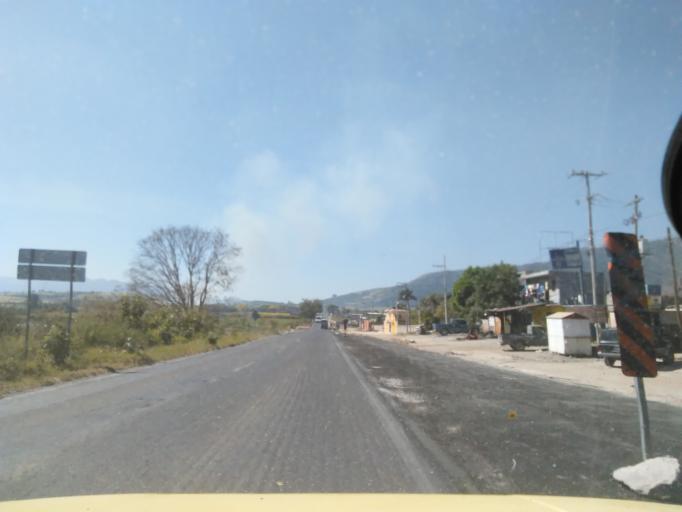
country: MX
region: Nayarit
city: Xalisco
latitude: 21.4346
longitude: -104.8998
